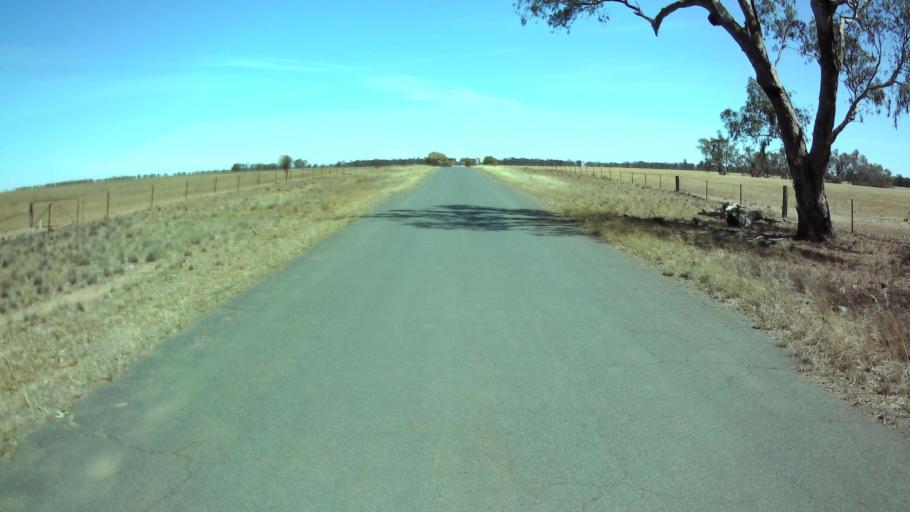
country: AU
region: New South Wales
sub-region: Weddin
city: Grenfell
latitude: -33.8497
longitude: 147.6958
